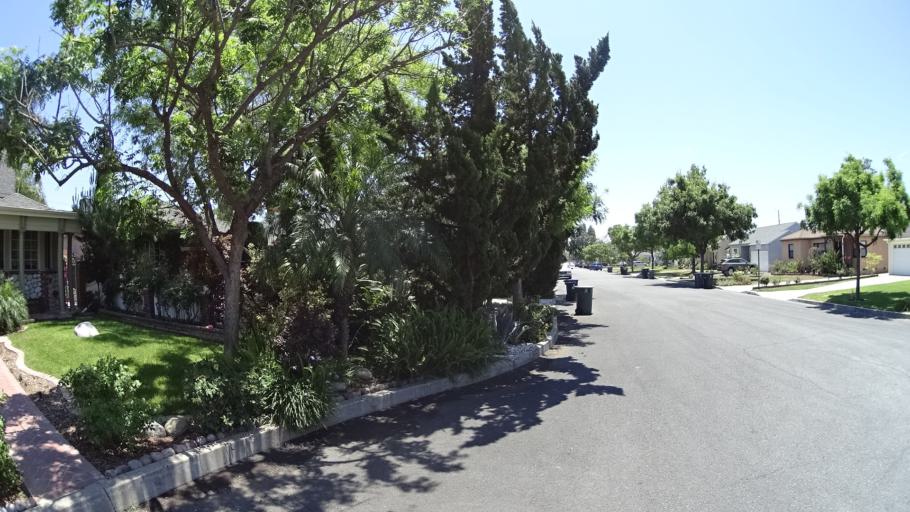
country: US
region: California
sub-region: Los Angeles County
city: Burbank
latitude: 34.1827
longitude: -118.3394
